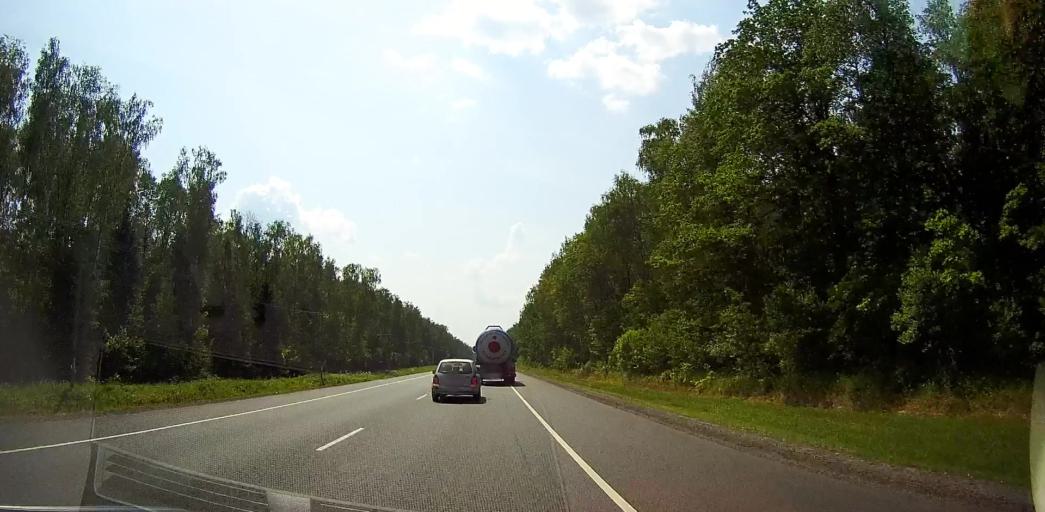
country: RU
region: Moskovskaya
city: Meshcherino
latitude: 55.2166
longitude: 38.3935
